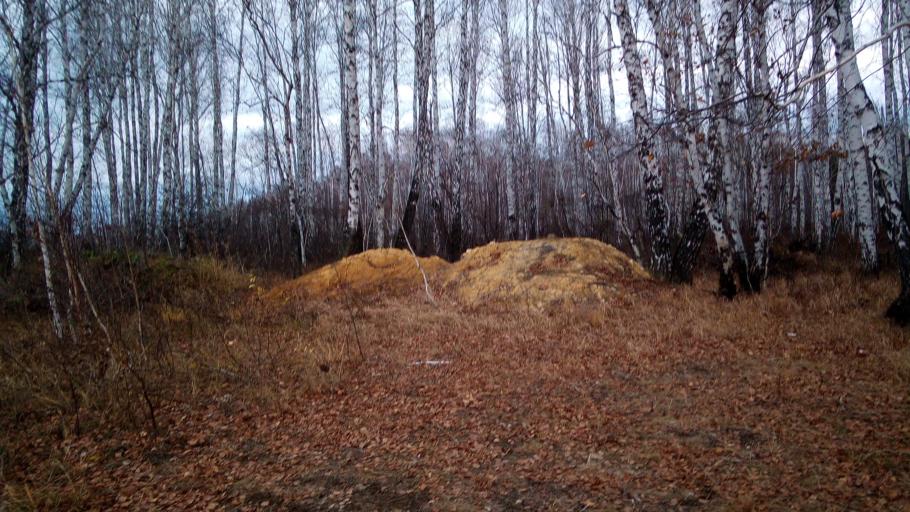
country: RU
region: Chelyabinsk
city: Sargazy
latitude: 55.1249
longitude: 61.2510
